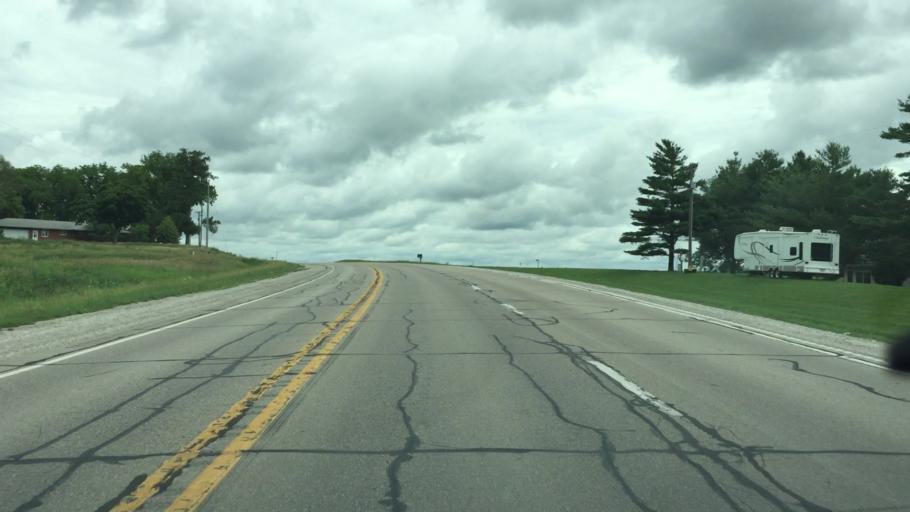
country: US
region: Iowa
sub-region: Jasper County
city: Monroe
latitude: 41.5458
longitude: -93.0974
